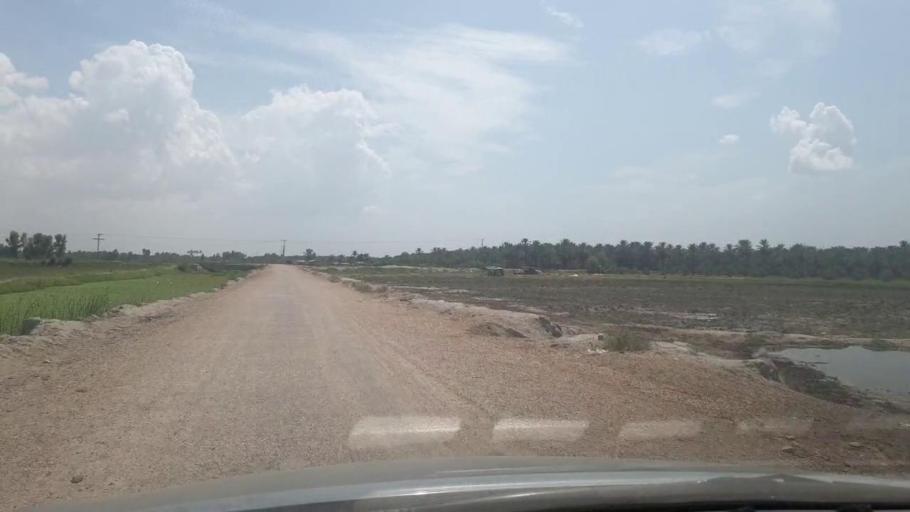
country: PK
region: Sindh
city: Khairpur
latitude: 27.4828
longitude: 68.8130
